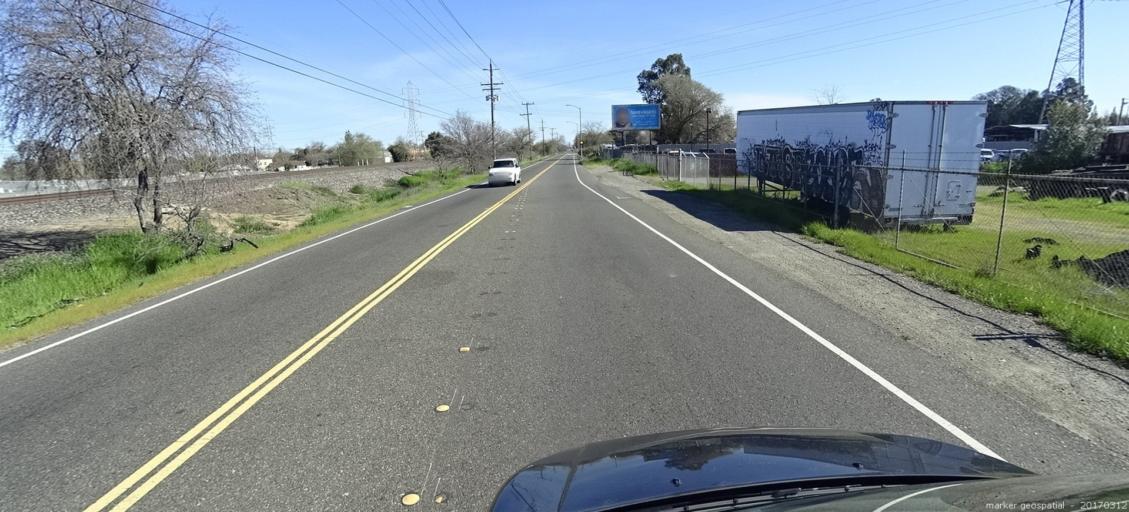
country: US
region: California
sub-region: Sacramento County
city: Arden-Arcade
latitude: 38.6230
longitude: -121.4218
